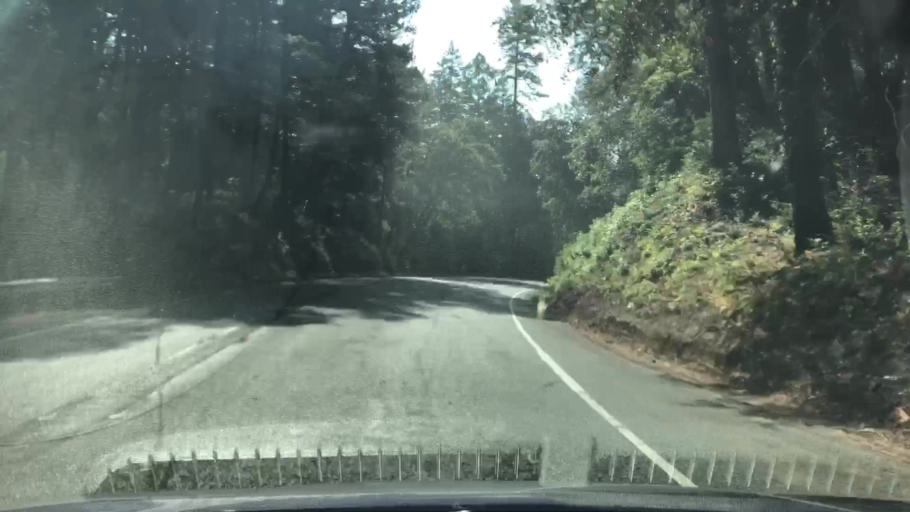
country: US
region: California
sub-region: Lake County
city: Middletown
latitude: 38.6731
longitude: -122.5911
